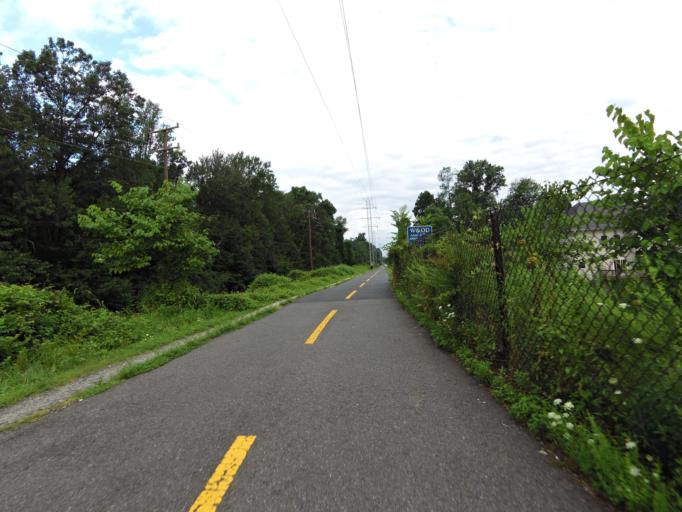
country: US
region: Virginia
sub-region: Fairfax County
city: Dunn Loring
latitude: 38.8907
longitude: -77.2188
